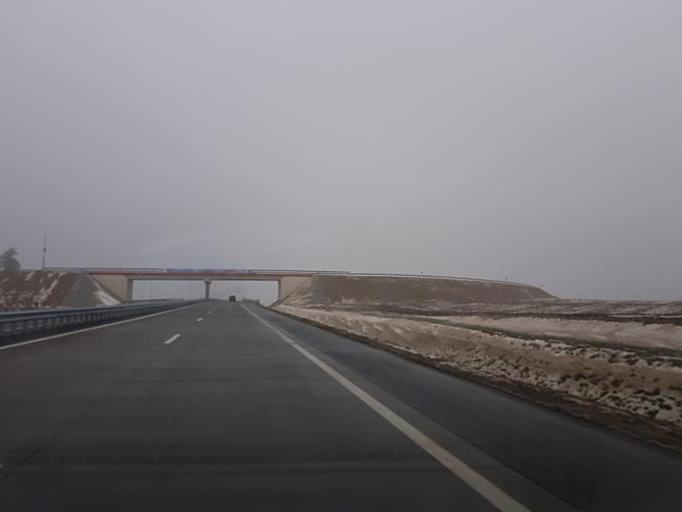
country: BY
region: Minsk
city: Atolina
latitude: 53.7309
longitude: 27.4226
